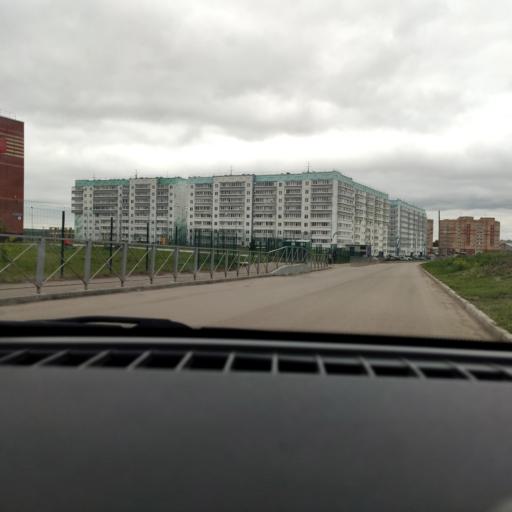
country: RU
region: Perm
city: Froly
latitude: 57.9230
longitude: 56.2836
